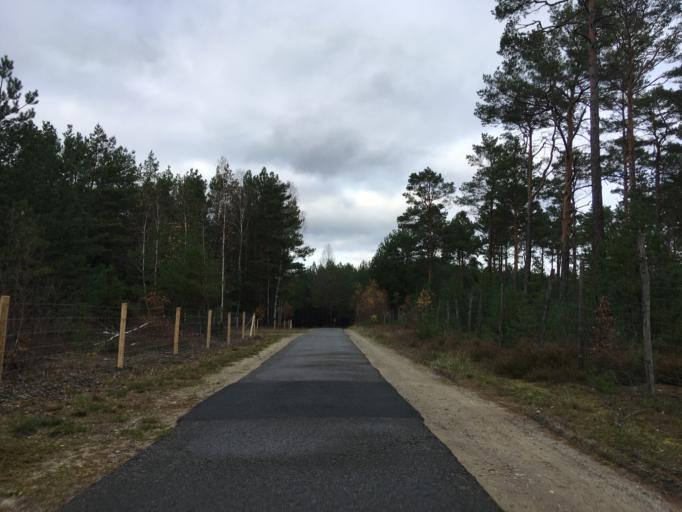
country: DE
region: Brandenburg
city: Tauer
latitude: 51.9932
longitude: 14.5153
